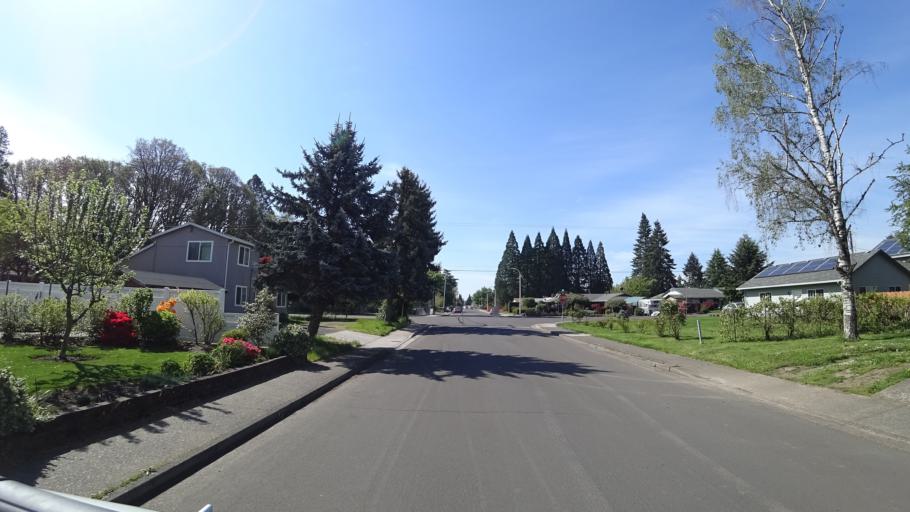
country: US
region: Oregon
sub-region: Washington County
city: Hillsboro
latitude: 45.5247
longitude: -122.9443
